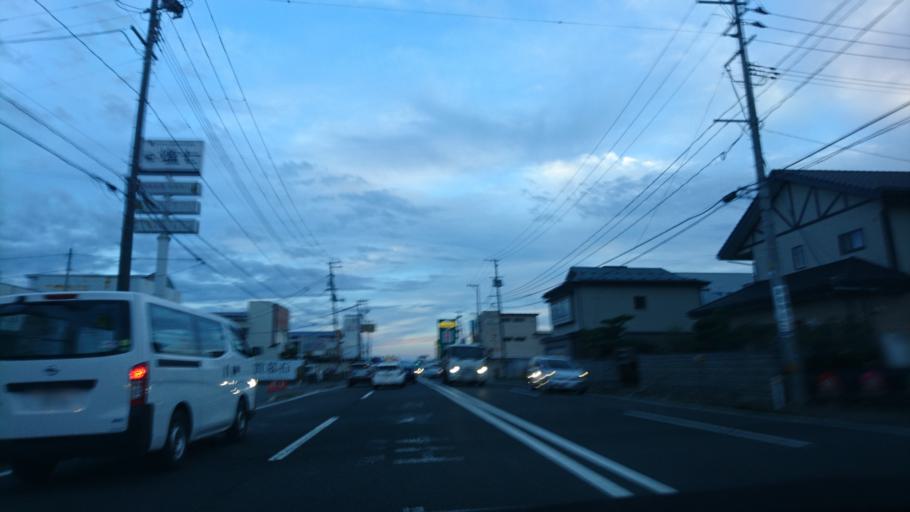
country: JP
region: Iwate
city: Morioka-shi
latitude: 39.6657
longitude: 141.1586
